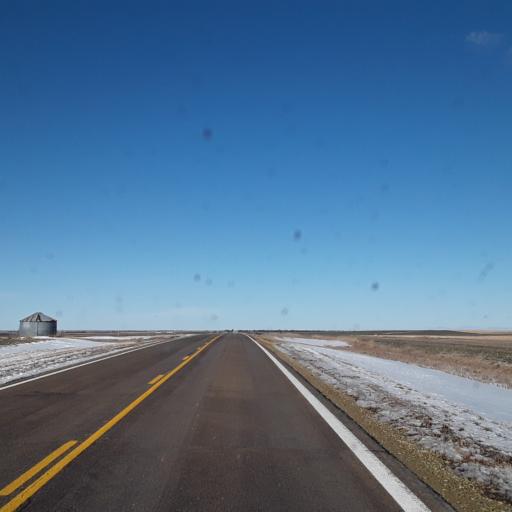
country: US
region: Kansas
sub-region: Mitchell County
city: Beloit
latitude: 39.3657
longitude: -98.1162
